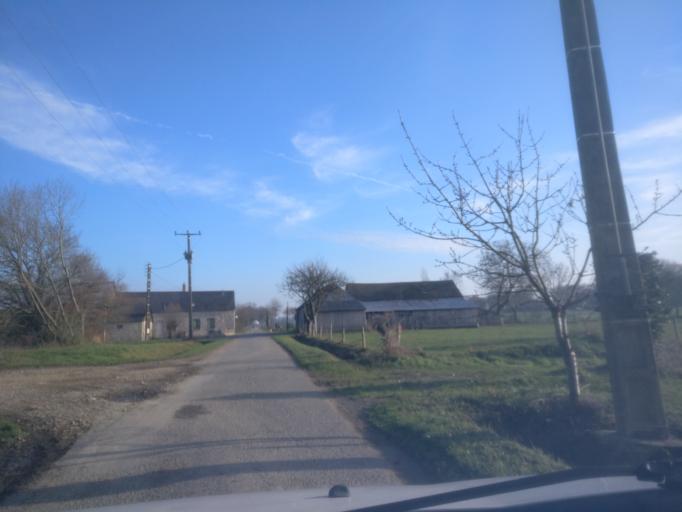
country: FR
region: Brittany
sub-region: Departement d'Ille-et-Vilaine
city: Livre-sur-Changeon
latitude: 48.2183
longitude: -1.3182
